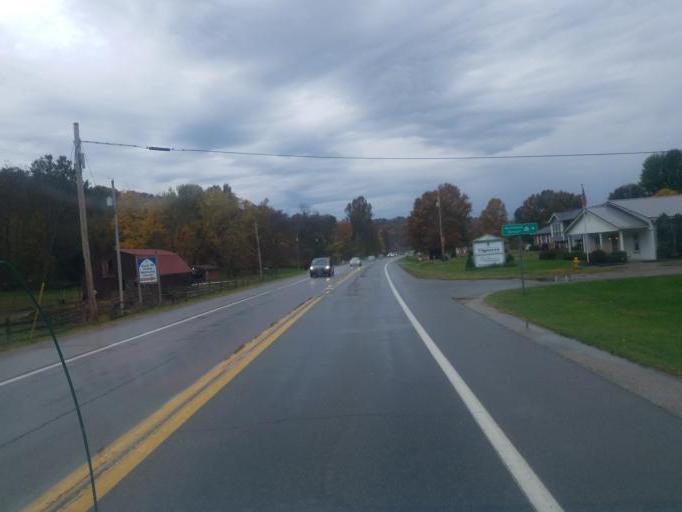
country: US
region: West Virginia
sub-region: Wood County
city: Boaz
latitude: 39.3682
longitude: -81.4841
